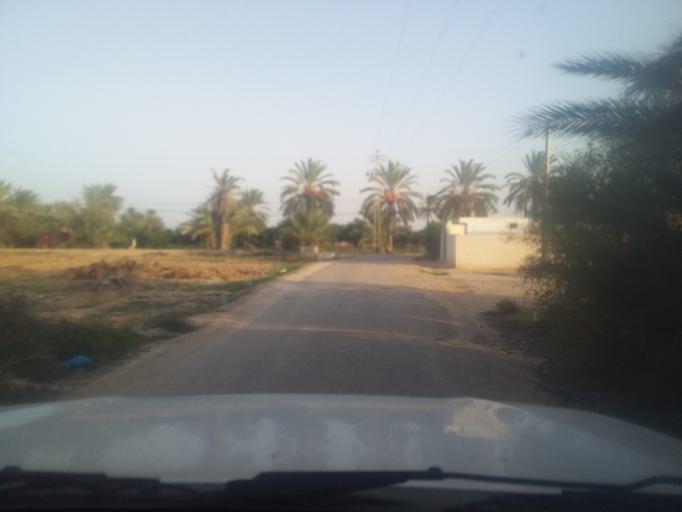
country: TN
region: Qabis
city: Gabes
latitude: 33.6192
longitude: 10.2984
